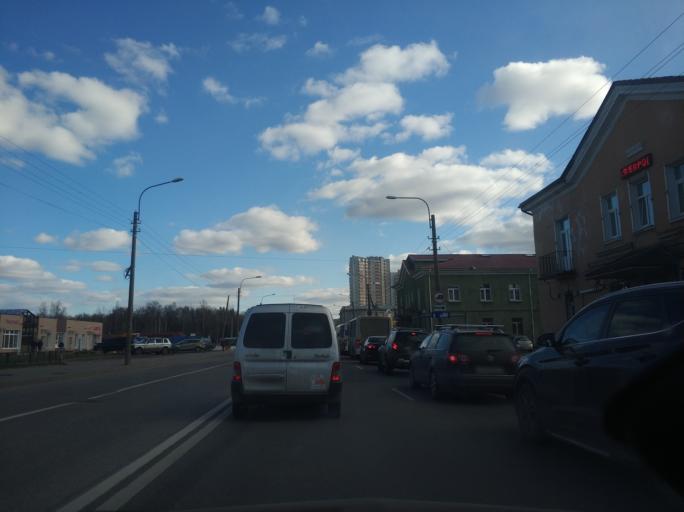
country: RU
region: St.-Petersburg
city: Krasnogvargeisky
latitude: 59.9634
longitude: 30.4870
